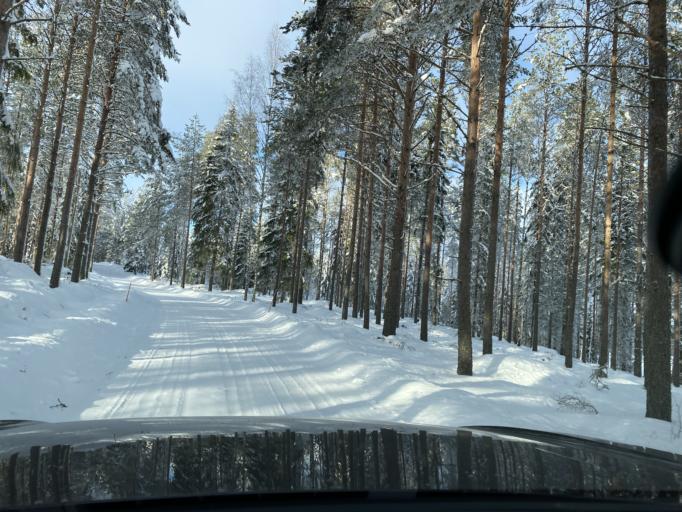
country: FI
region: Pirkanmaa
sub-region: Lounais-Pirkanmaa
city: Punkalaidun
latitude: 61.0723
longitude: 23.2363
